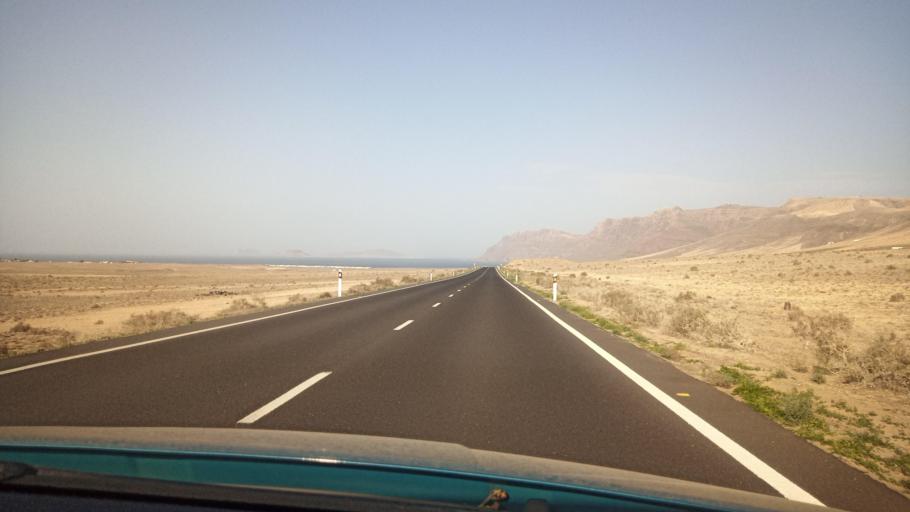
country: ES
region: Canary Islands
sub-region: Provincia de Las Palmas
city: Teguise
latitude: 29.0749
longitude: -13.5787
